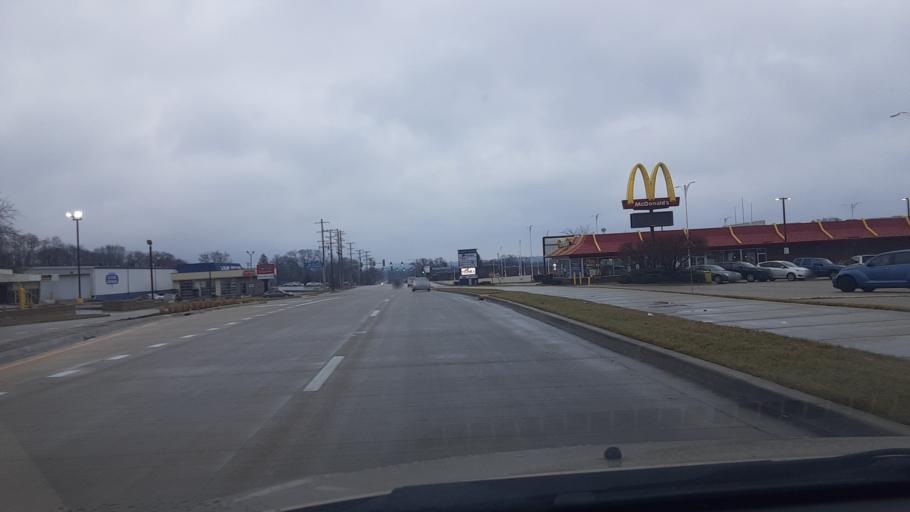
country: US
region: Illinois
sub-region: Winnebago County
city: Loves Park
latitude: 42.3157
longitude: -89.0761
